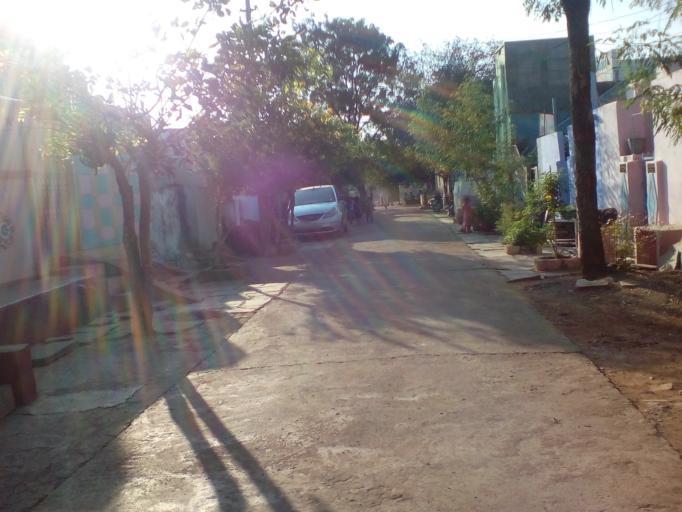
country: IN
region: Andhra Pradesh
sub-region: Kurnool
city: Nandikotkur
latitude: 15.8496
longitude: 78.2643
